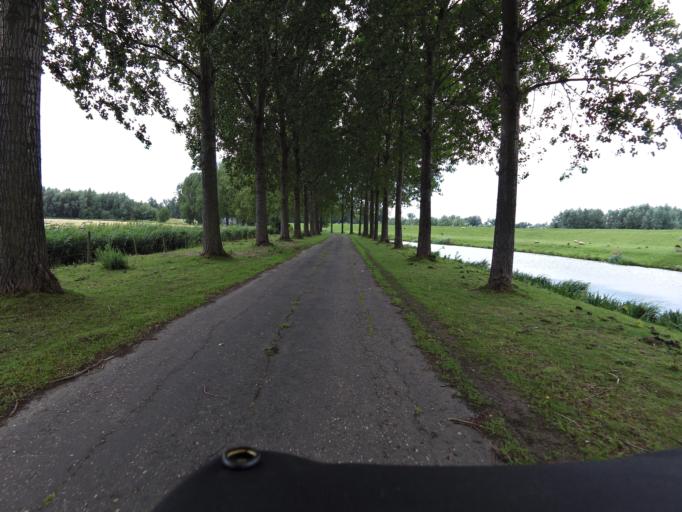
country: NL
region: North Brabant
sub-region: Gemeente Moerdijk
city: Willemstad
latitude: 51.7179
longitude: 4.4755
